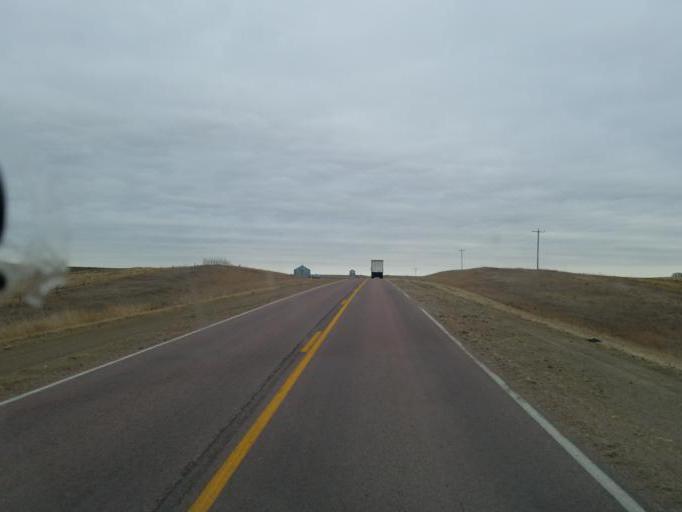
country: US
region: Nebraska
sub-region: Cedar County
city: Hartington
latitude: 42.4673
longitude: -97.1854
